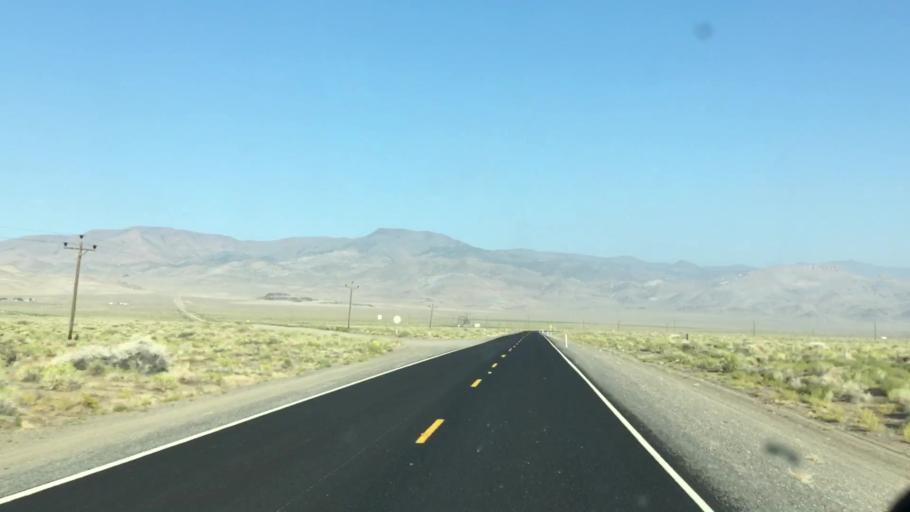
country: US
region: Nevada
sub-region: Lyon County
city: Fernley
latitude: 39.6490
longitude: -119.3201
